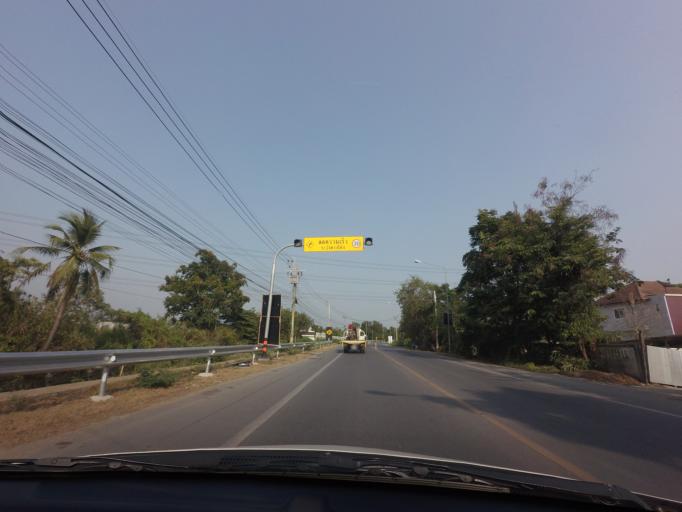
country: TH
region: Bangkok
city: Thawi Watthana
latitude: 13.8098
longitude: 100.3557
